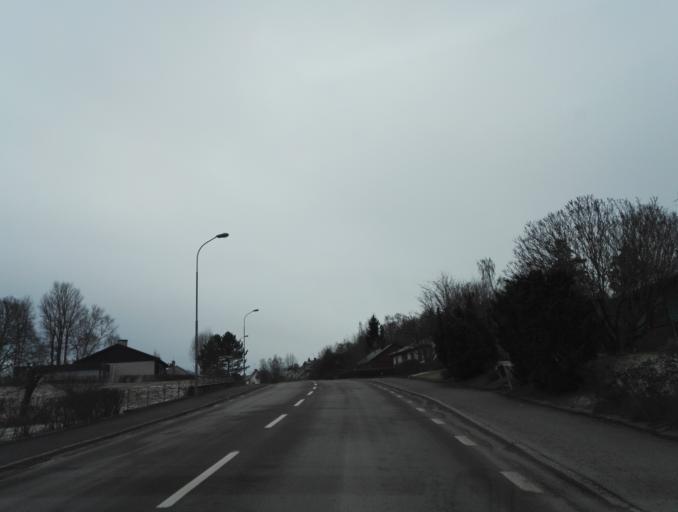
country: SE
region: Kalmar
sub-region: Hultsfreds Kommun
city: Virserum
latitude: 57.3127
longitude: 15.5848
